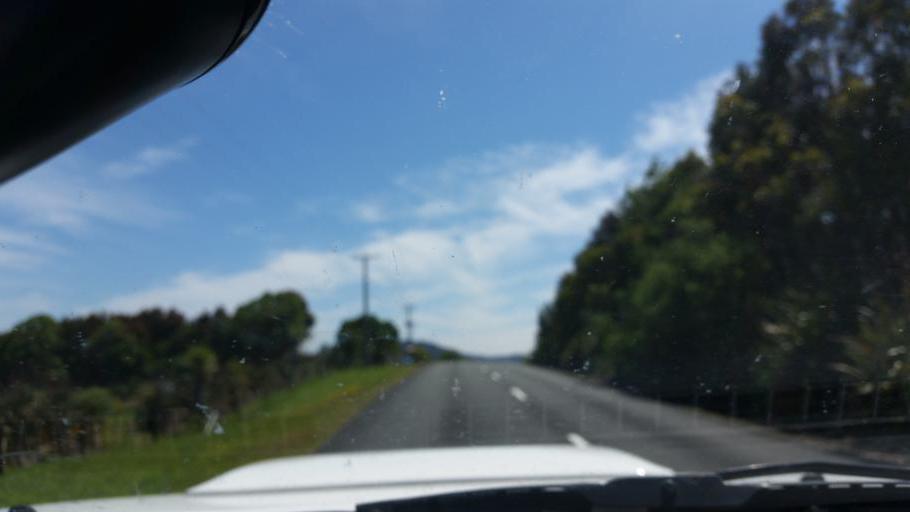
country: NZ
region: Auckland
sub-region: Auckland
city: Wellsford
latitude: -36.1769
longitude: 174.4149
